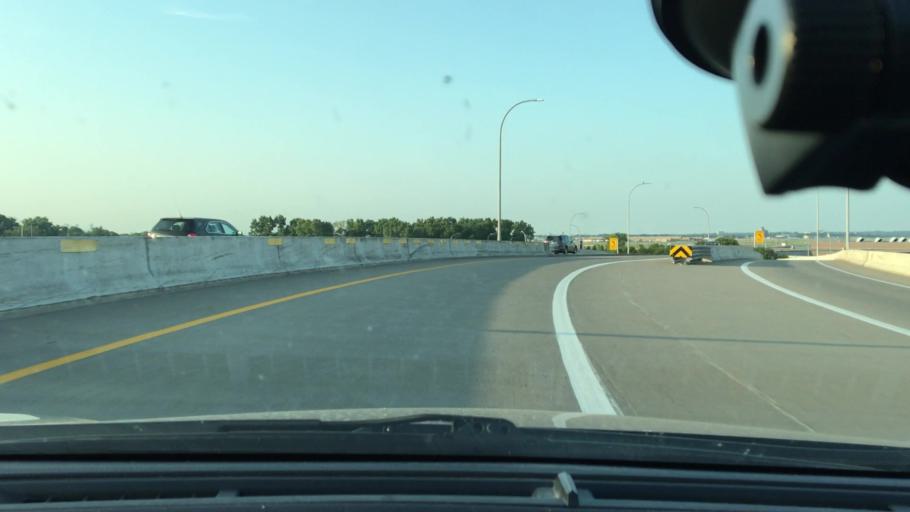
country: US
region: Minnesota
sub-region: Hennepin County
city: Richfield
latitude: 44.8608
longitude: -93.2466
